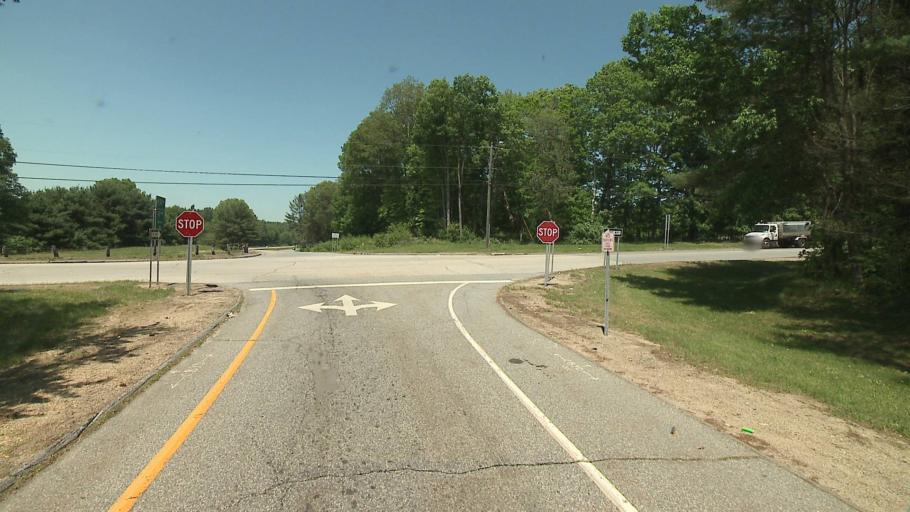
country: US
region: Connecticut
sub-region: Windham County
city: Putnam
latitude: 41.9092
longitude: -71.8904
